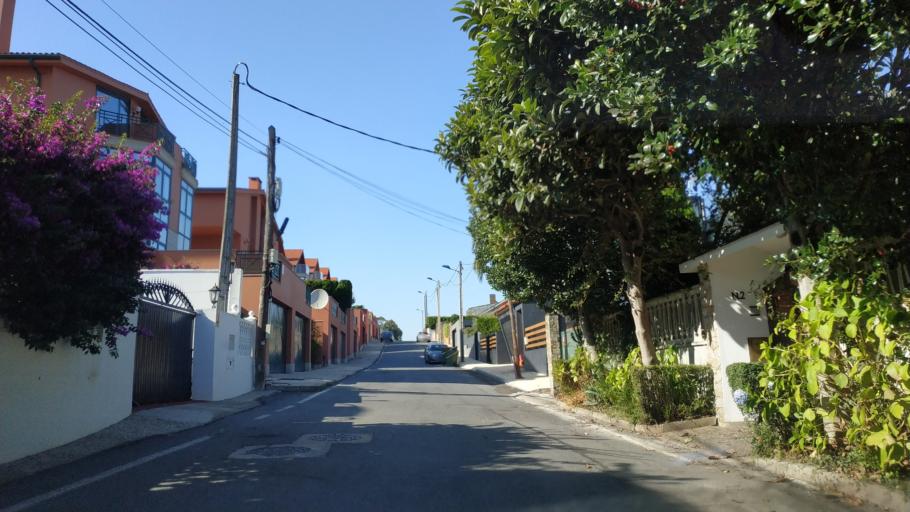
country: ES
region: Galicia
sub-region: Provincia da Coruna
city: Culleredo
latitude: 43.3231
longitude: -8.3881
